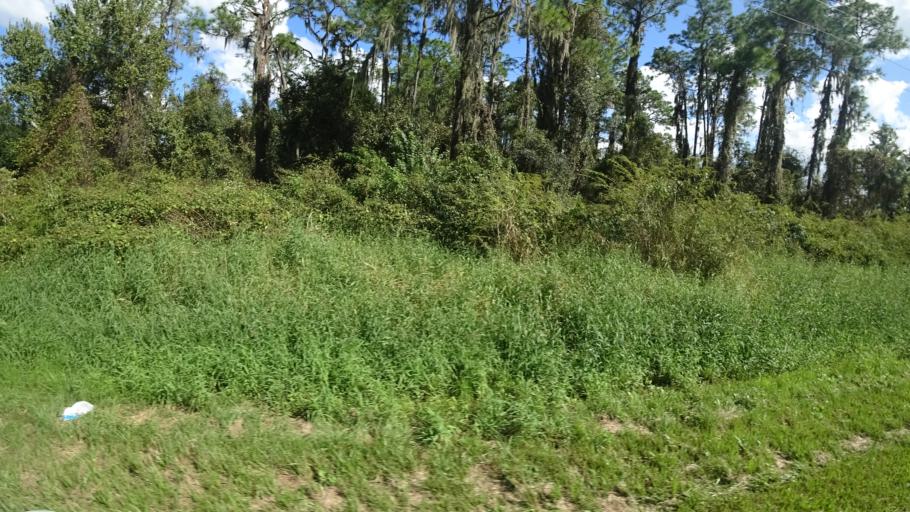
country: US
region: Florida
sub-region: Sarasota County
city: Lake Sarasota
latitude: 27.3817
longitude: -82.1395
